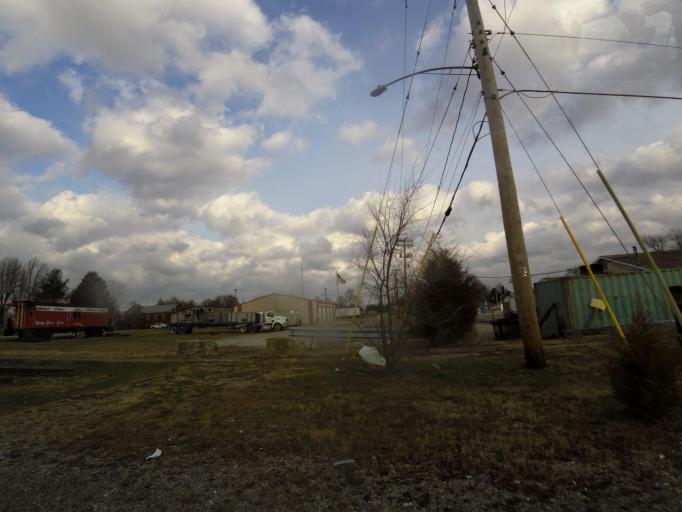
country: US
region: Illinois
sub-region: Fayette County
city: Ramsey
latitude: 39.1402
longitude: -89.1089
